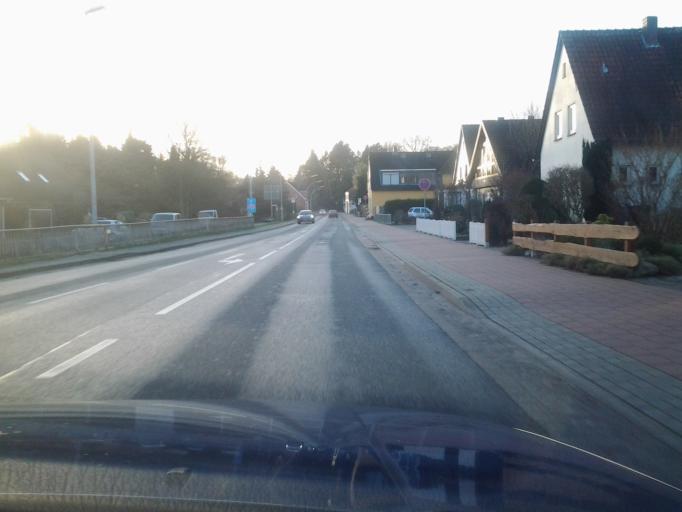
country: DE
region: Lower Saxony
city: Osterholz-Scharmbeck
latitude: 53.2233
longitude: 8.8073
